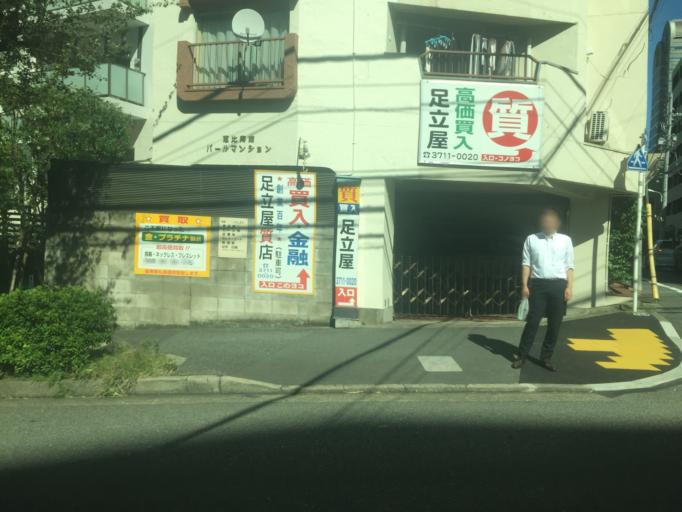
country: JP
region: Tokyo
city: Tokyo
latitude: 35.6453
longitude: 139.7084
